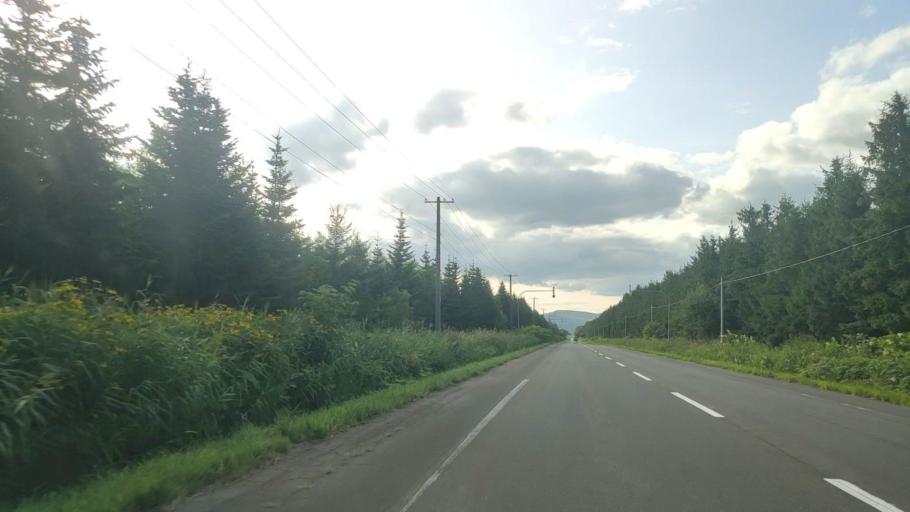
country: JP
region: Hokkaido
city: Makubetsu
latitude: 44.8866
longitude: 142.0089
